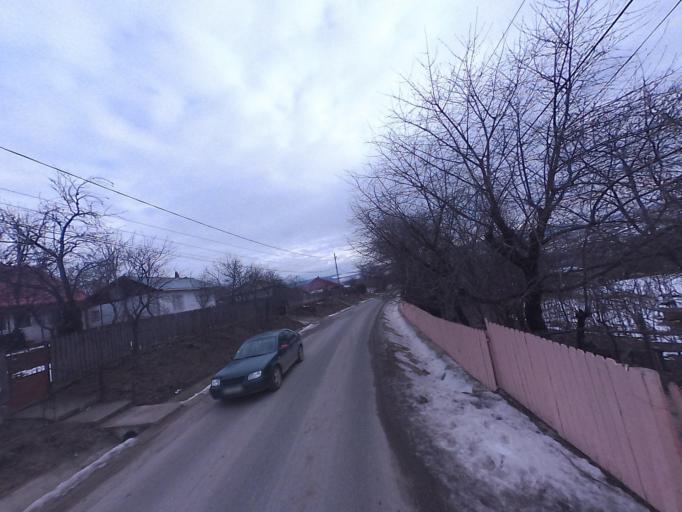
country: RO
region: Iasi
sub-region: Comuna Tibanesti
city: Glodenii Gandului
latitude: 46.9791
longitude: 27.2988
